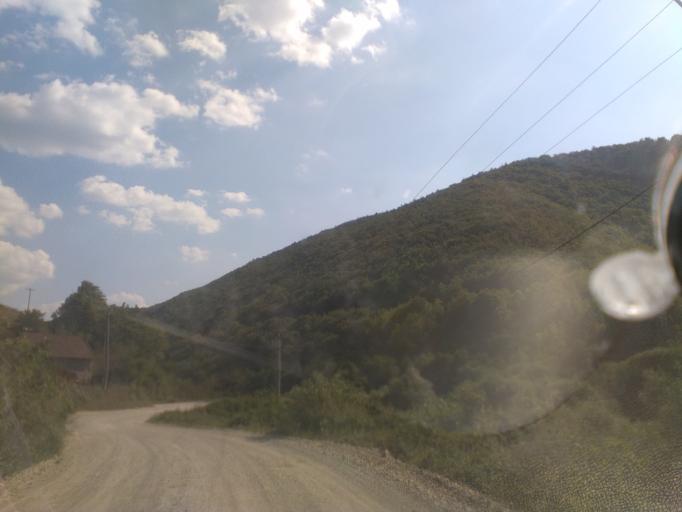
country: BA
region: Federation of Bosnia and Herzegovina
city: Orasac
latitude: 44.5107
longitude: 16.1277
